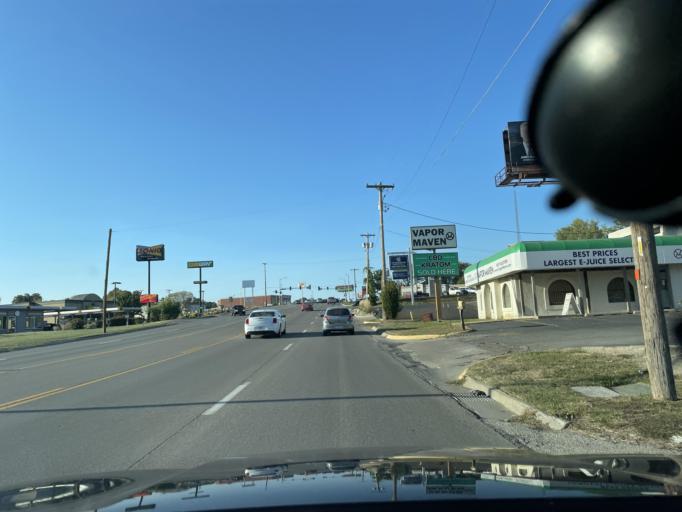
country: US
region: Missouri
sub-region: Andrew County
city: Country Club Village
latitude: 39.7977
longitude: -94.8137
